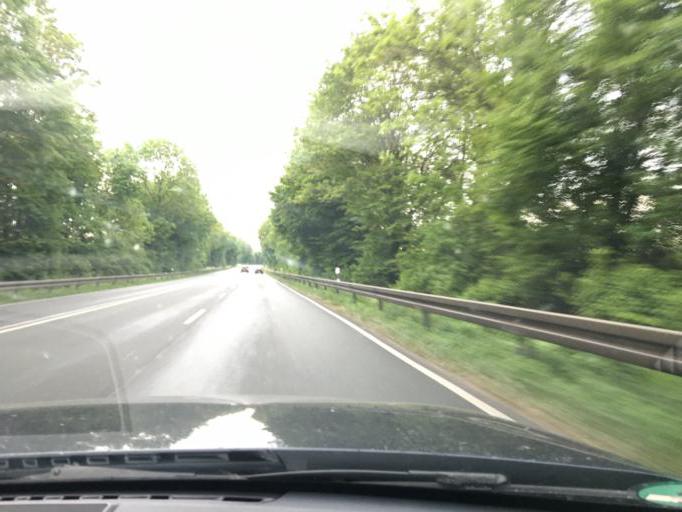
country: DE
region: North Rhine-Westphalia
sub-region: Regierungsbezirk Munster
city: Greven
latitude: 52.1091
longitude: 7.6198
